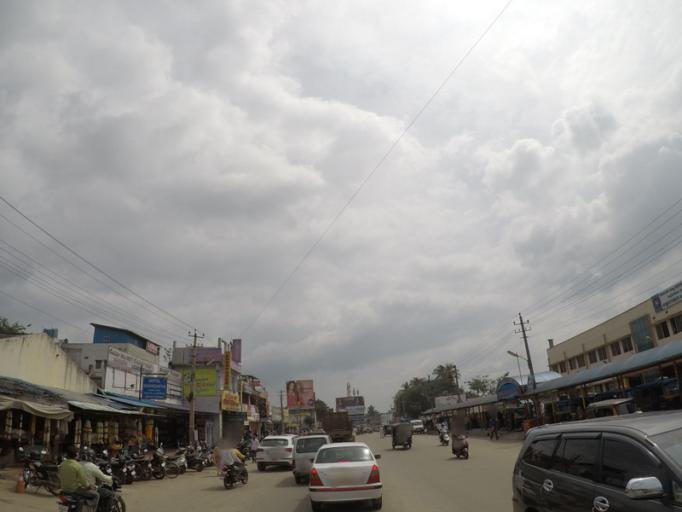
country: IN
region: Karnataka
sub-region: Chikmagalur
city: Chikmagalur
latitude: 13.3183
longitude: 75.7721
